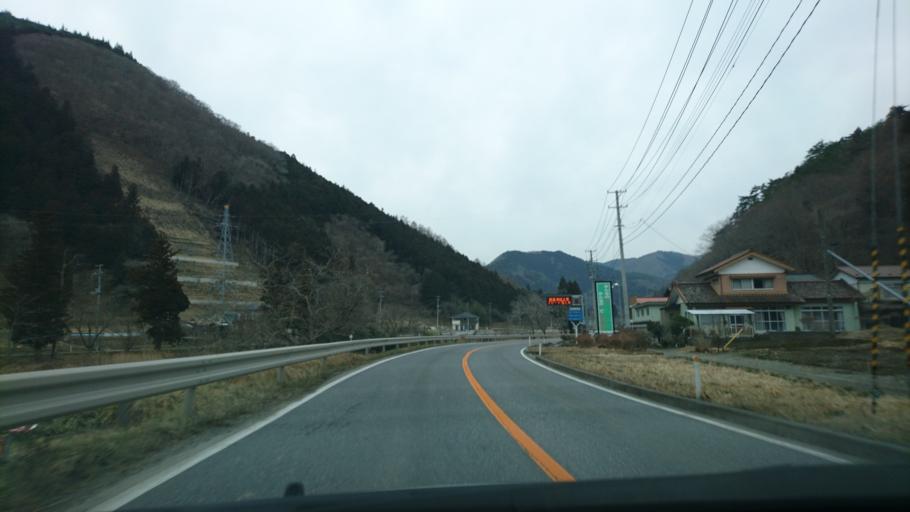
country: JP
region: Iwate
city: Tono
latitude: 39.1443
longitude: 141.5486
